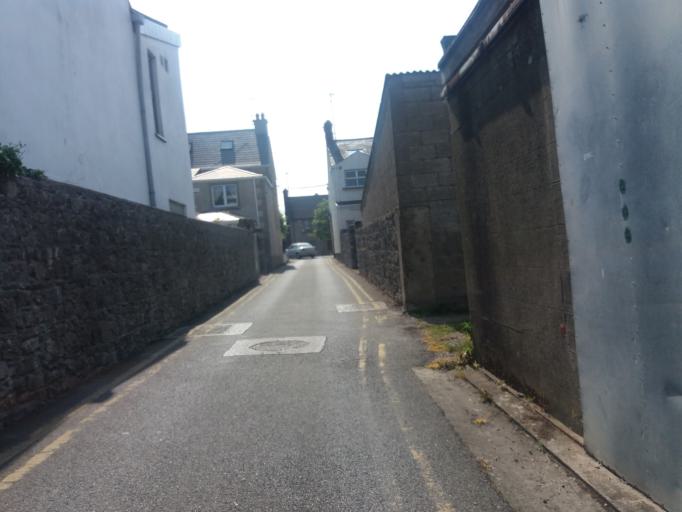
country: IE
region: Leinster
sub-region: Fingal County
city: Skerries
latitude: 53.5769
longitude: -6.1044
